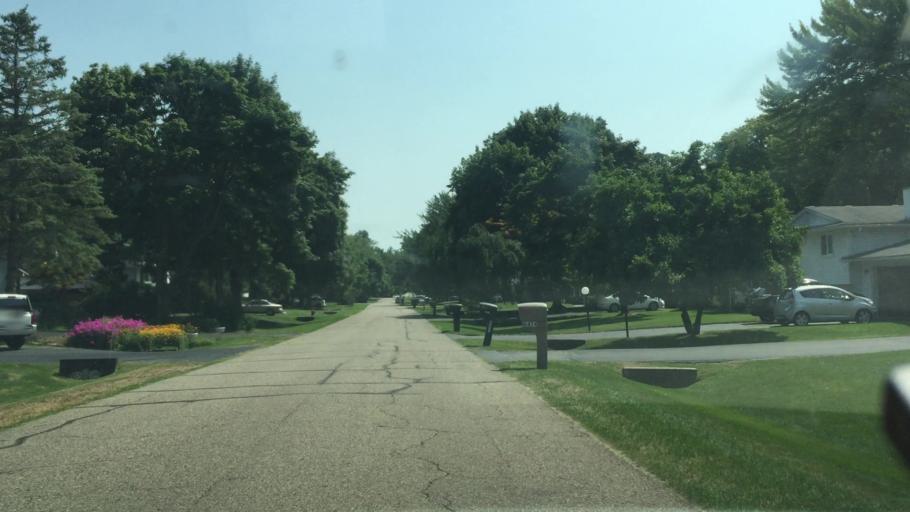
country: US
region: Michigan
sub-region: Oakland County
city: West Bloomfield Township
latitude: 42.5386
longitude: -83.3551
